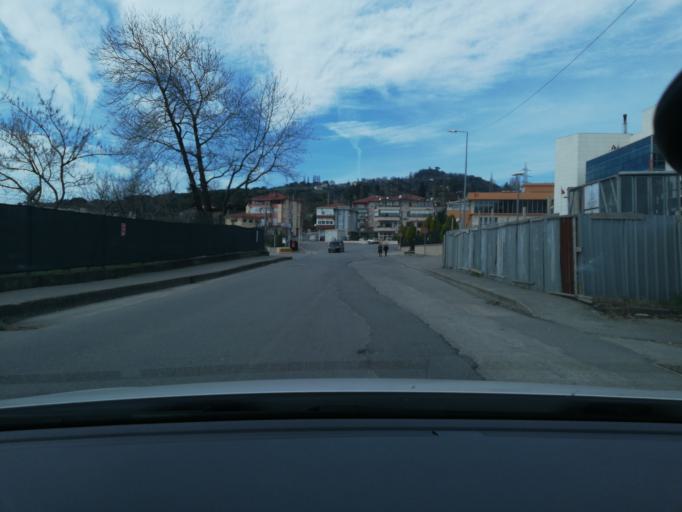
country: TR
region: Zonguldak
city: Eregli
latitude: 41.2905
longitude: 31.4077
